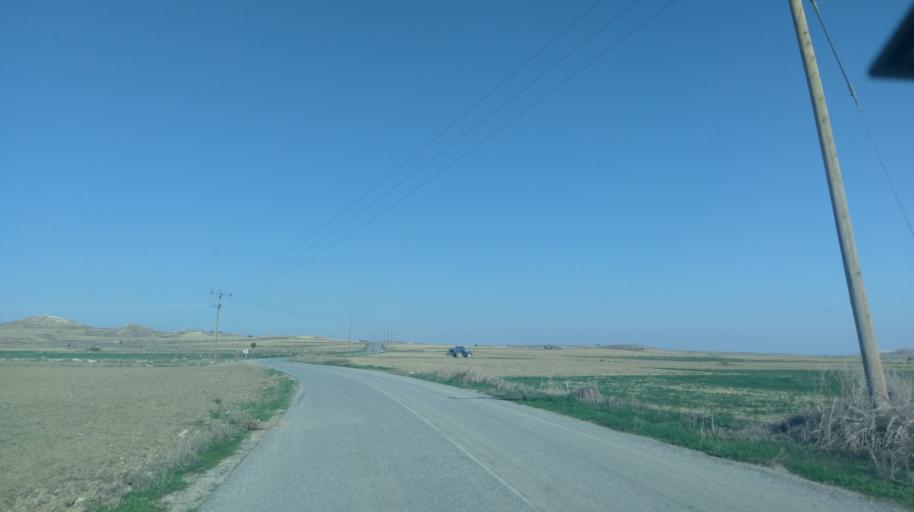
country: CY
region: Lefkosia
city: Lympia
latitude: 35.0386
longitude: 33.4784
